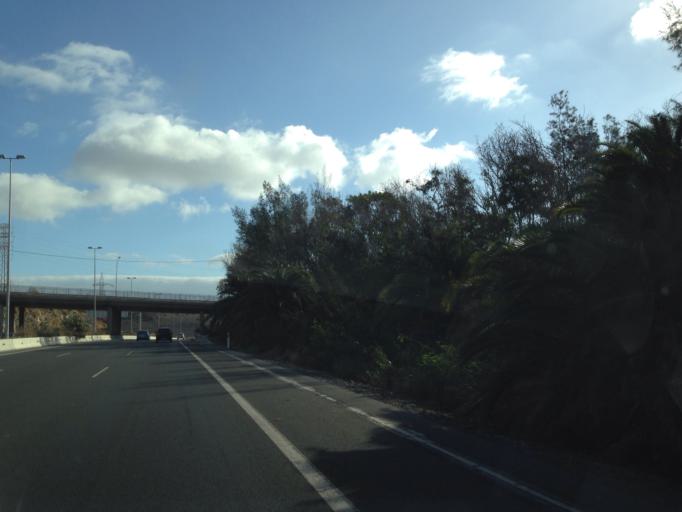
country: ES
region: Canary Islands
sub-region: Provincia de Las Palmas
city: Maspalomas
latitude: 27.7722
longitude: -15.5839
